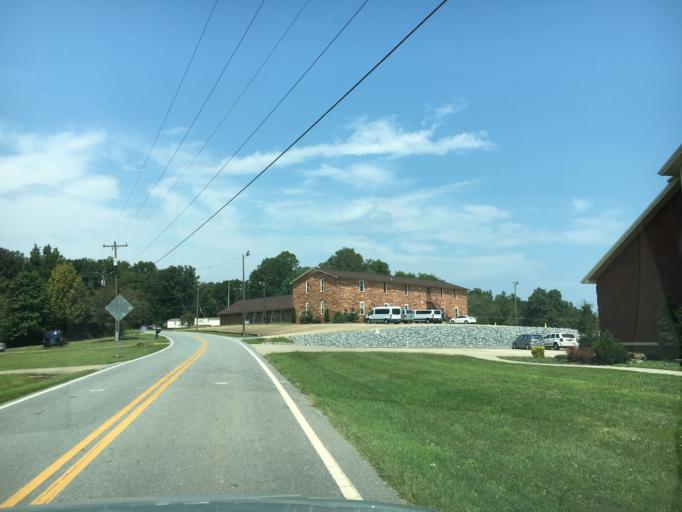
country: US
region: North Carolina
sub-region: McDowell County
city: Marion
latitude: 35.7015
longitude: -81.9134
